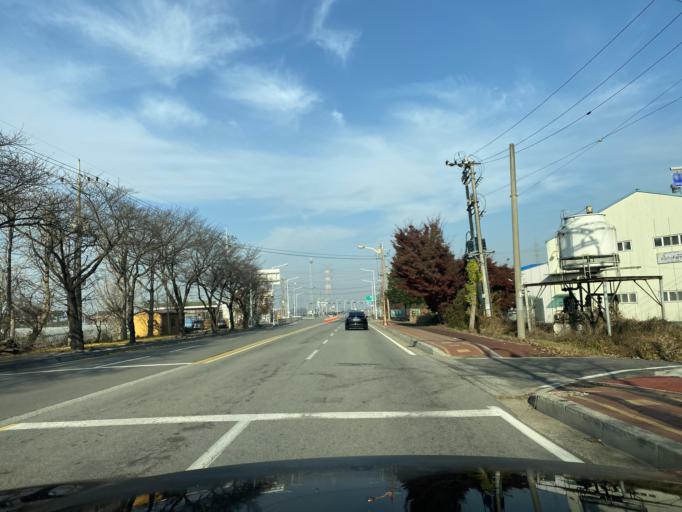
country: KR
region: Chungcheongnam-do
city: Yesan
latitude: 36.7374
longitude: 126.8607
